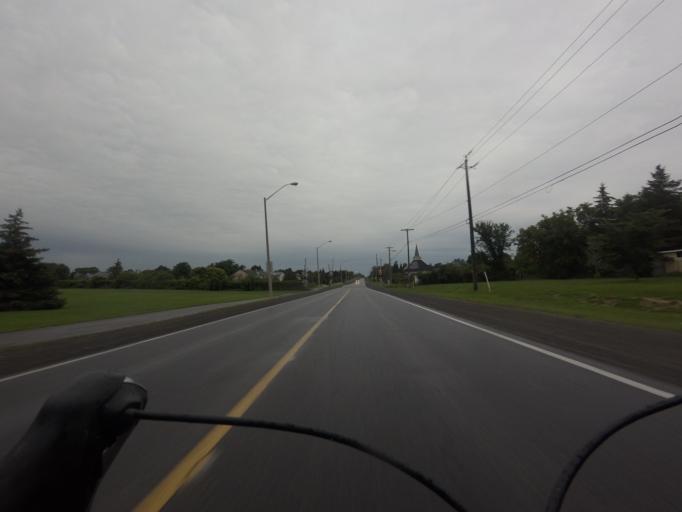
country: CA
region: Ontario
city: Bells Corners
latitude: 45.2716
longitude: -75.7569
